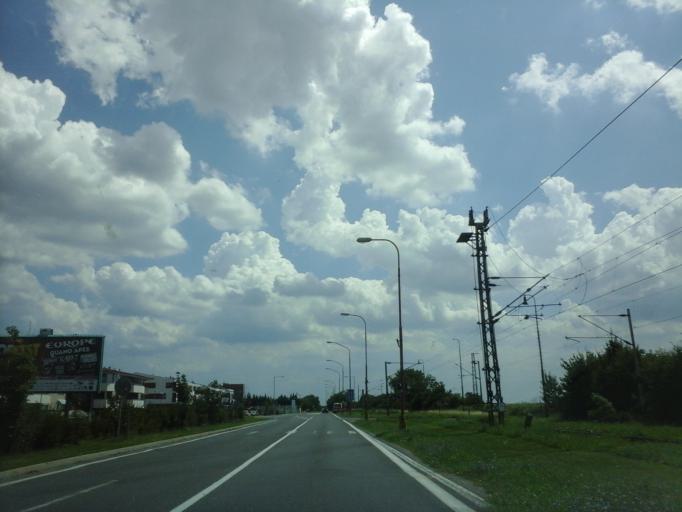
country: AT
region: Burgenland
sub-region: Politischer Bezirk Neusiedl am See
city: Deutsch Jahrndorf
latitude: 48.0443
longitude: 17.1547
